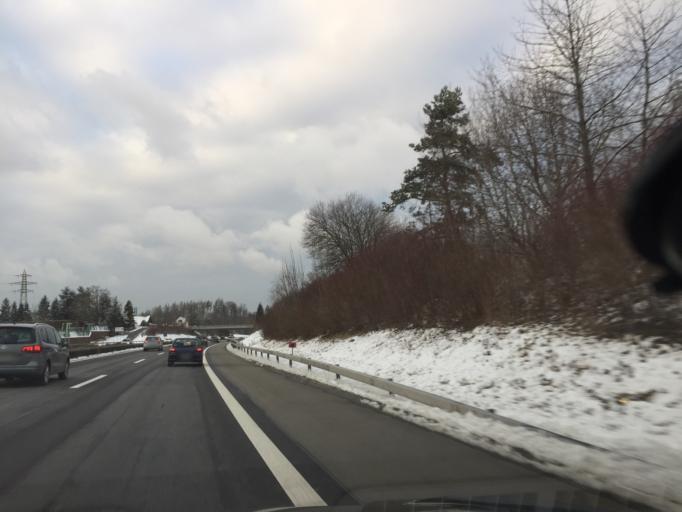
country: CH
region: Zurich
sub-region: Bezirk Horgen
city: Thalwil / Berg
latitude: 47.2894
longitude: 8.5519
